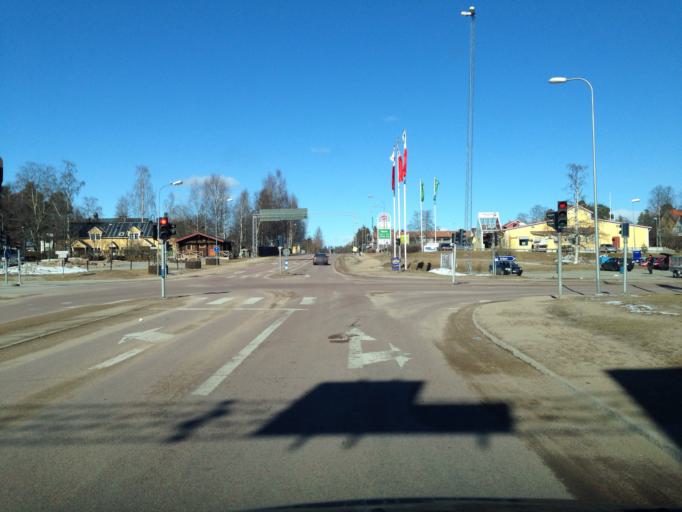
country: SE
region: Jaemtland
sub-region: Harjedalens Kommun
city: Sveg
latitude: 62.0337
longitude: 14.3661
